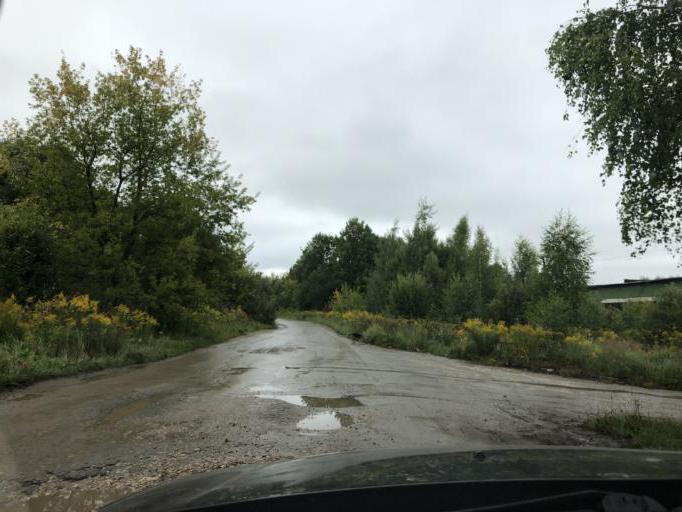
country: RU
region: Tula
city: Mendeleyevskiy
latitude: 54.1710
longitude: 37.5526
